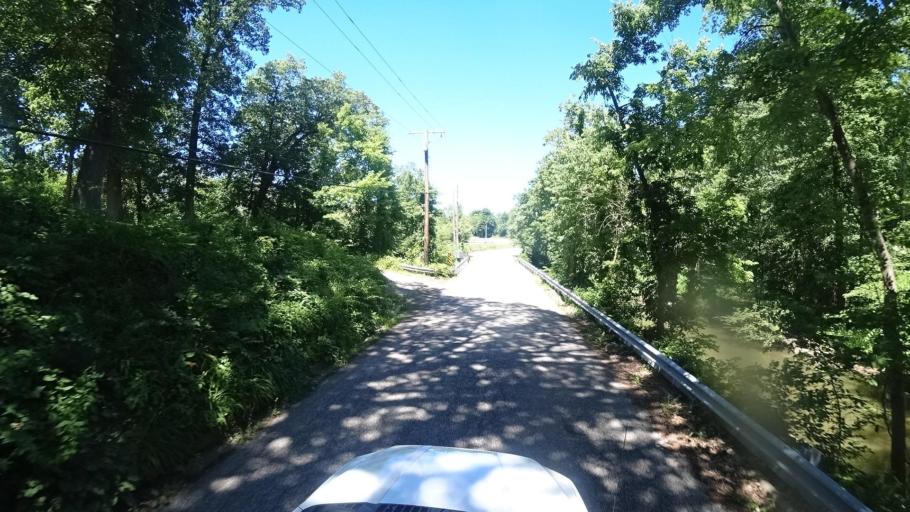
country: US
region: Indiana
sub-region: Porter County
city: Porter
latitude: 41.6214
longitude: -87.0868
